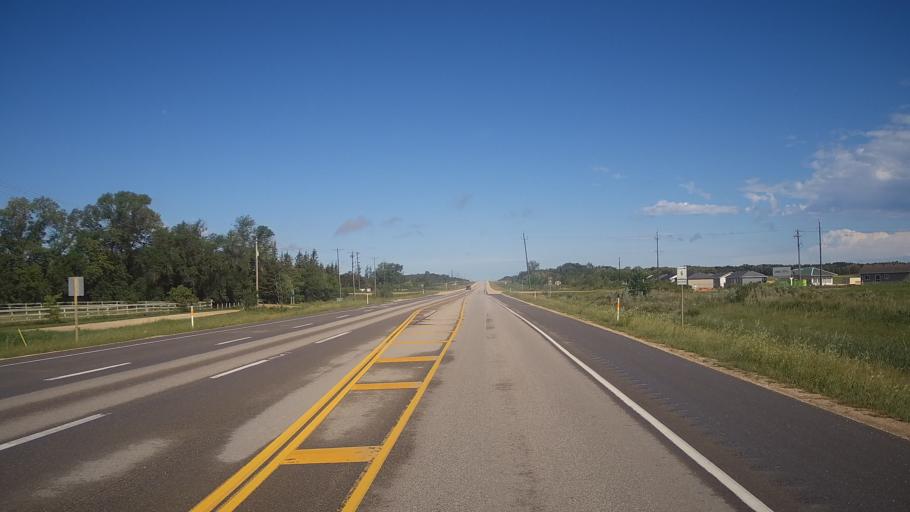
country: CA
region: Manitoba
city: Stonewall
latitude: 50.2102
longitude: -97.6666
